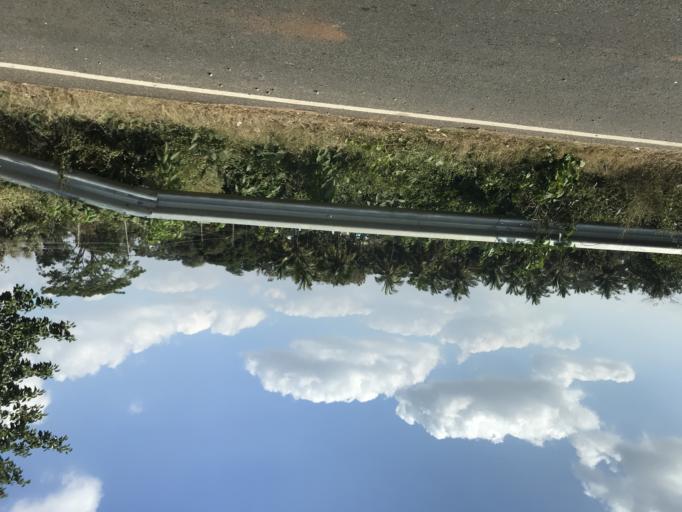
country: IN
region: Karnataka
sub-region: Bangalore Urban
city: Anekal
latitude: 12.8043
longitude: 77.5603
